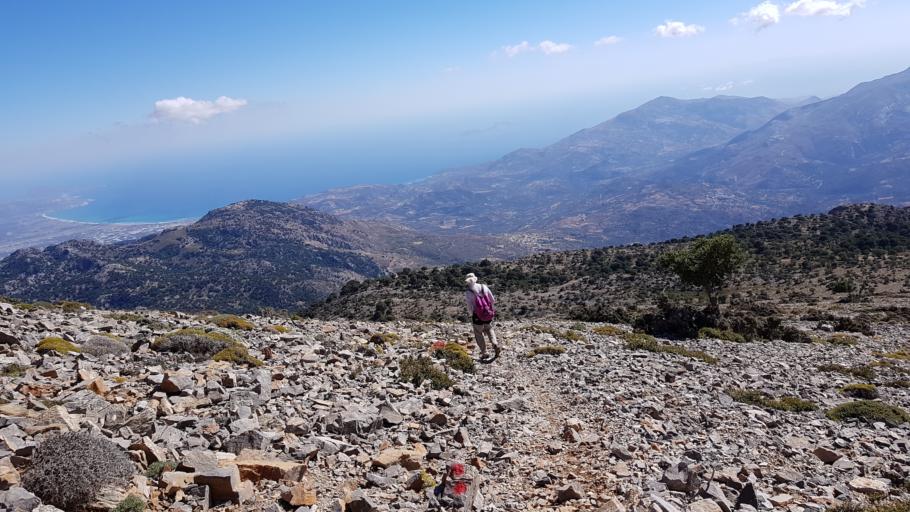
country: GR
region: Crete
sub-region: Nomos Rethymnis
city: Zoniana
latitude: 35.2089
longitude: 24.7679
